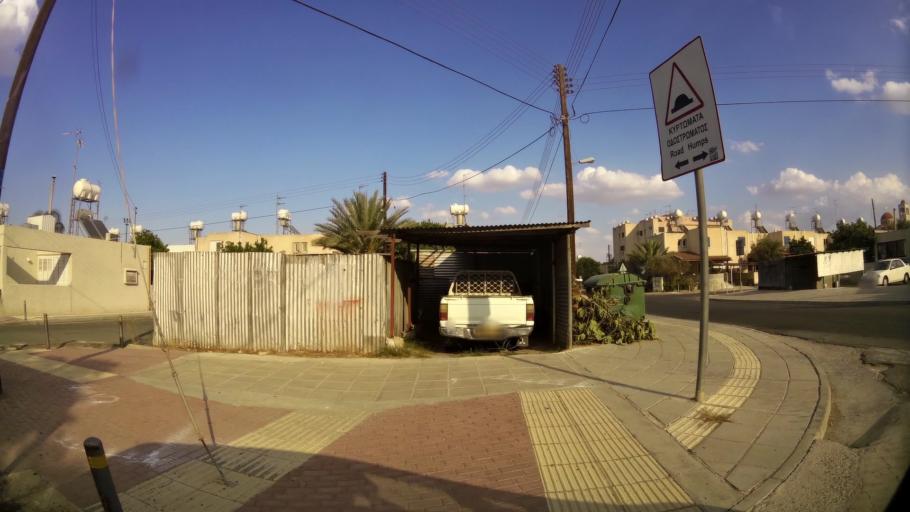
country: CY
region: Lefkosia
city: Kato Deftera
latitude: 35.1059
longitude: 33.2898
